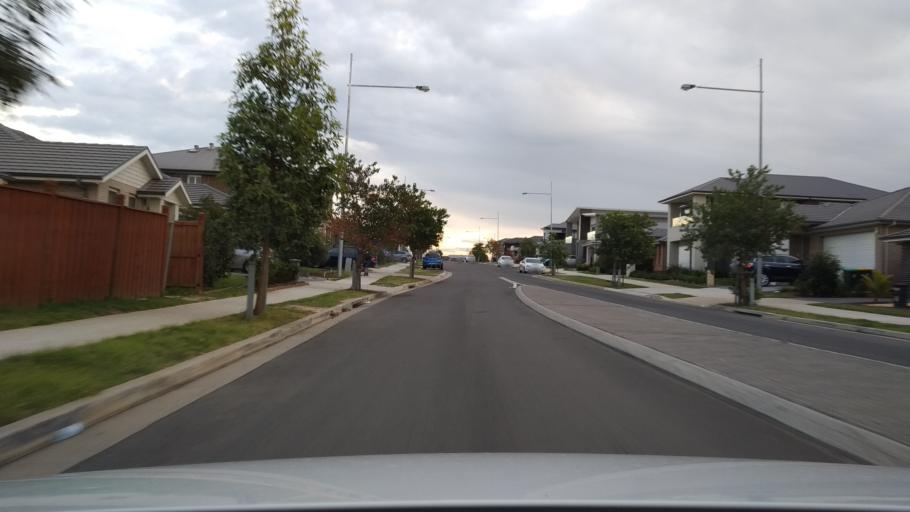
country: AU
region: New South Wales
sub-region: Camden
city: Narellan
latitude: -33.9990
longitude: 150.7344
